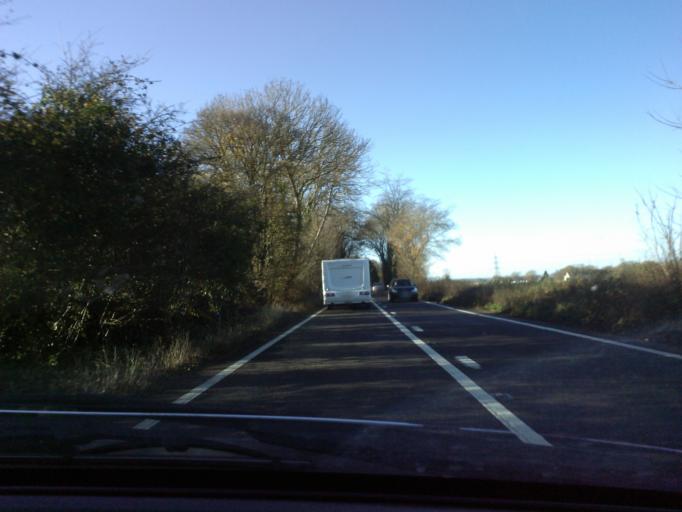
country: GB
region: England
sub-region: Dorset
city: Lytchett Matravers
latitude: 50.7863
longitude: -2.0506
